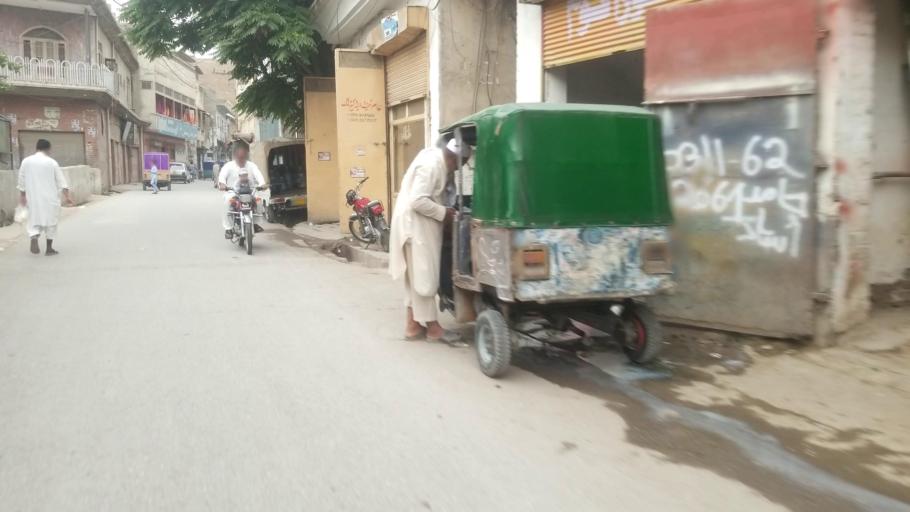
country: PK
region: Khyber Pakhtunkhwa
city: Peshawar
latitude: 33.9995
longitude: 71.5662
